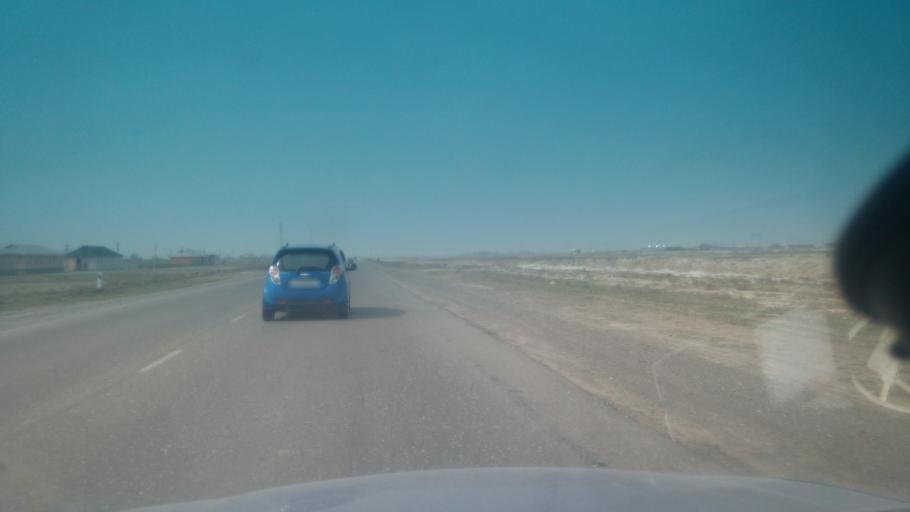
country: UZ
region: Jizzax
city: Dashtobod
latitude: 40.1676
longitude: 68.6101
